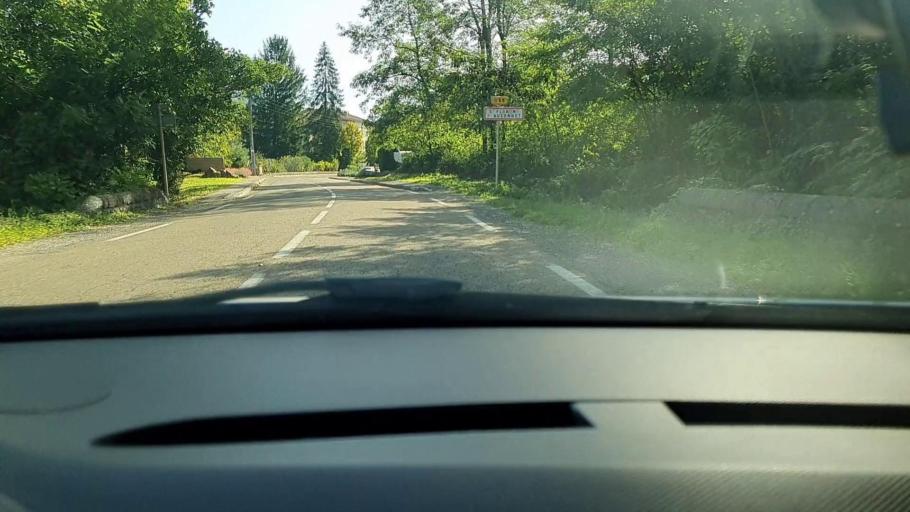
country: FR
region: Languedoc-Roussillon
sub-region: Departement du Gard
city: Saint-Florent-sur-Auzonnet
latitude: 44.2458
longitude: 4.0972
